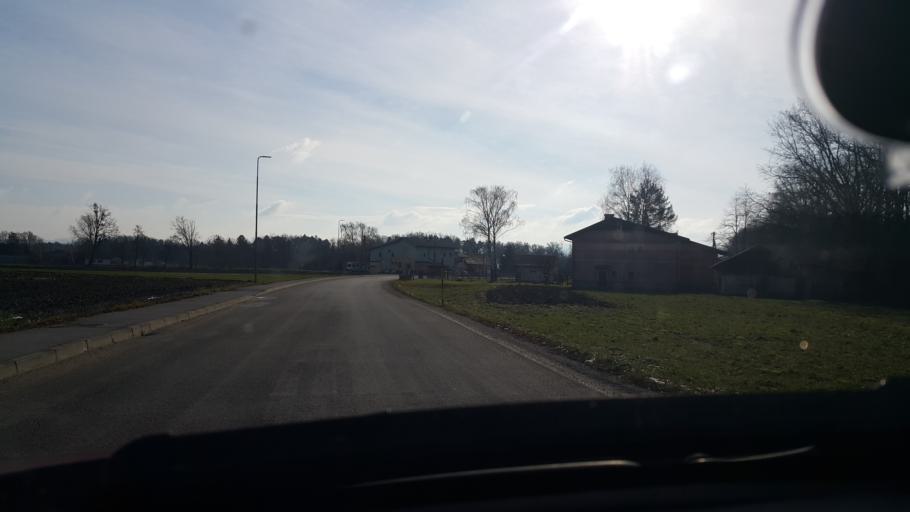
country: SI
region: Slovenska Bistrica
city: Pragersko
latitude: 46.3894
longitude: 15.6297
